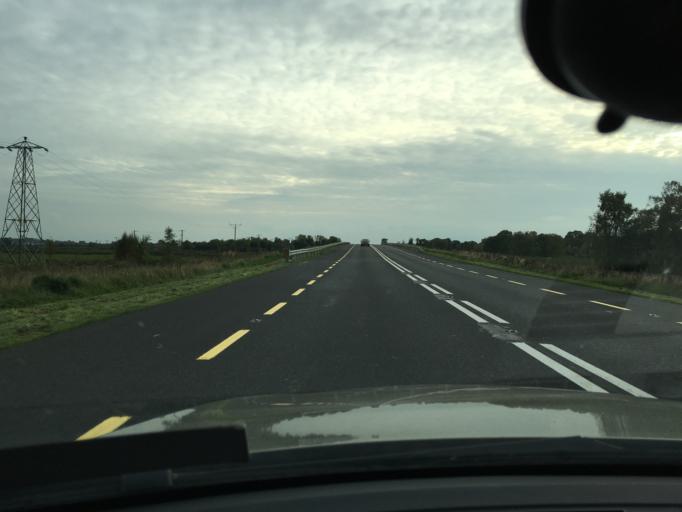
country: IE
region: Leinster
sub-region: An Longfort
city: Longford
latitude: 53.7383
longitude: -7.8154
